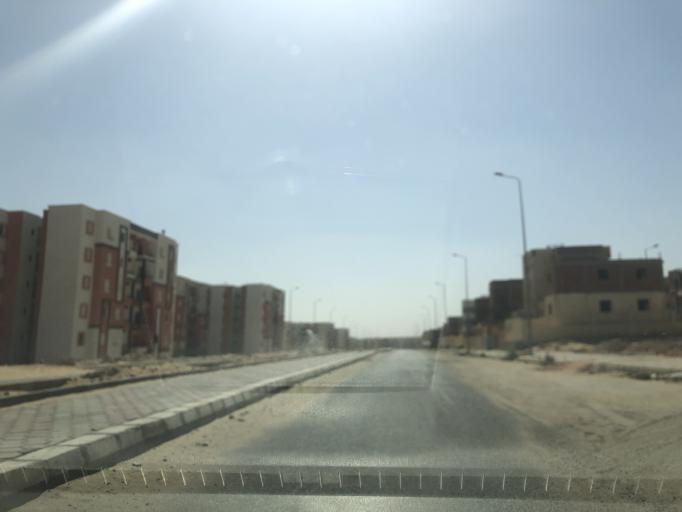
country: EG
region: Al Jizah
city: Madinat Sittah Uktubar
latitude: 29.9278
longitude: 31.0024
